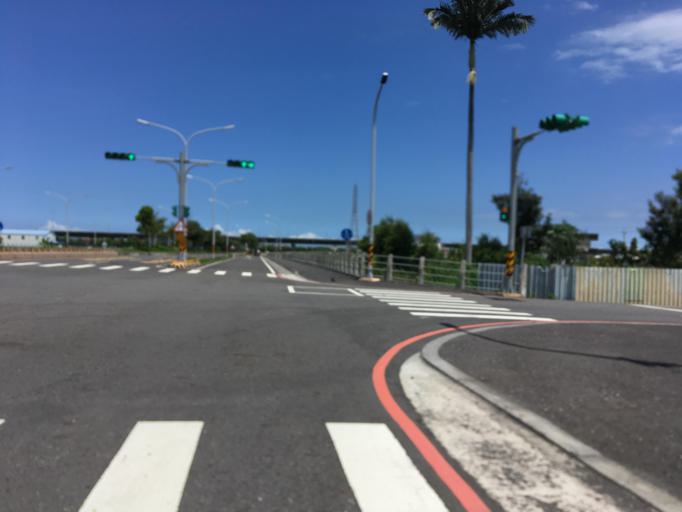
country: TW
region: Taiwan
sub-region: Yilan
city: Yilan
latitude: 24.6933
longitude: 121.7865
